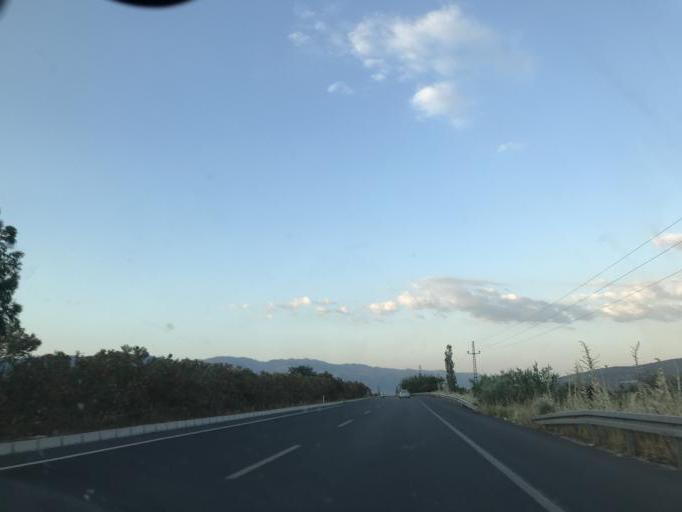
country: TR
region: Aydin
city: Horsunlu
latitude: 37.9269
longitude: 28.6532
